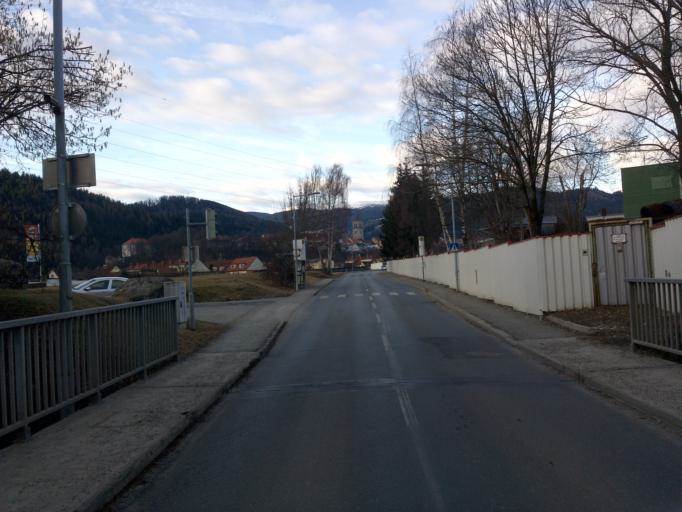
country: AT
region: Styria
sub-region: Politischer Bezirk Murtal
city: Judenburg
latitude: 47.1743
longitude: 14.6713
